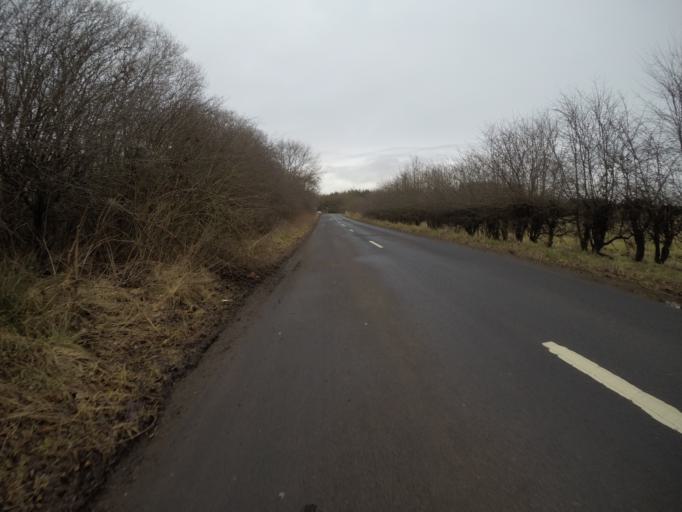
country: GB
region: Scotland
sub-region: North Ayrshire
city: Kilwinning
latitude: 55.6387
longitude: -4.6908
